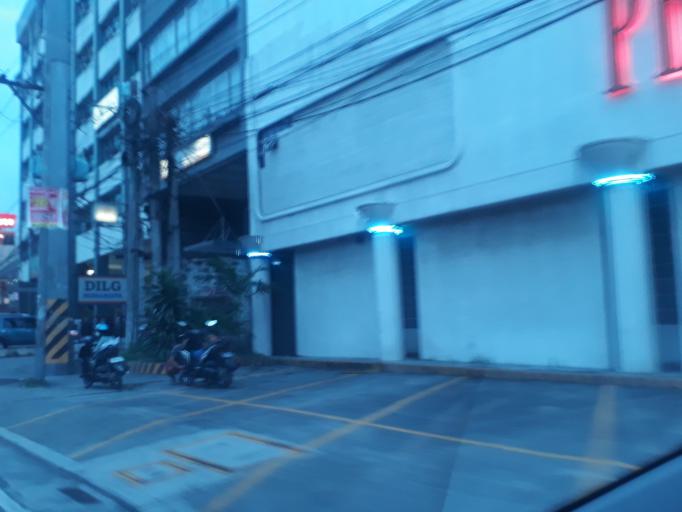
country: PH
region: Calabarzon
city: Del Monte
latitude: 14.6308
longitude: 121.0163
